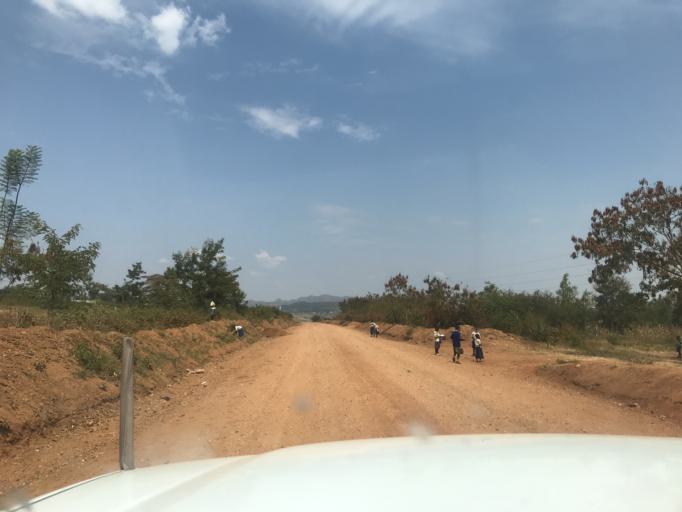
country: TZ
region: Mara
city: Nyamuswa
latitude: -1.9567
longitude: 33.9828
